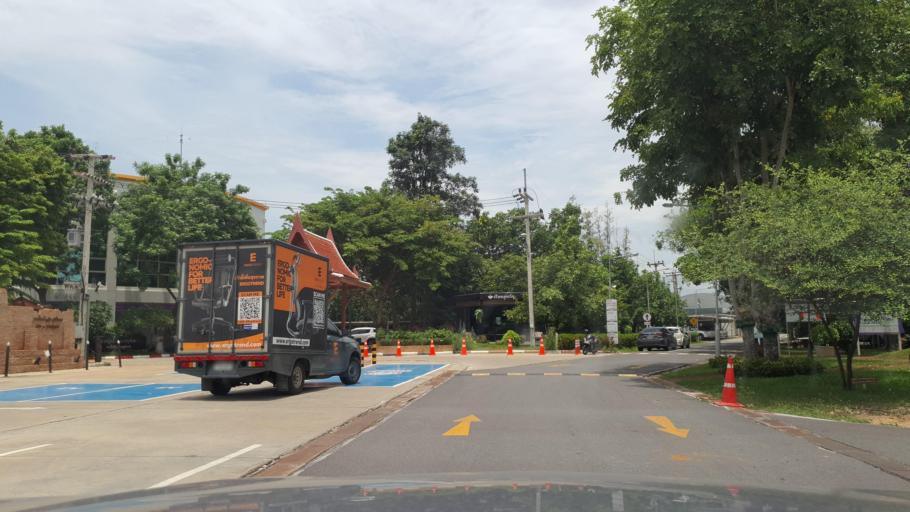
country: TH
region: Phra Nakhon Si Ayutthaya
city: Phra Nakhon Si Ayutthaya
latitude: 14.3836
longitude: 100.6035
